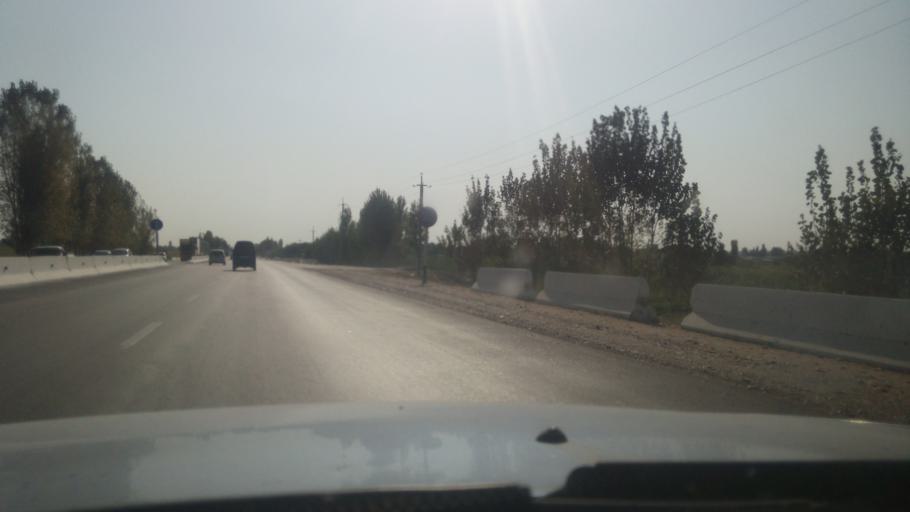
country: UZ
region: Toshkent
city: Urtaowul
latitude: 41.2157
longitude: 69.1290
